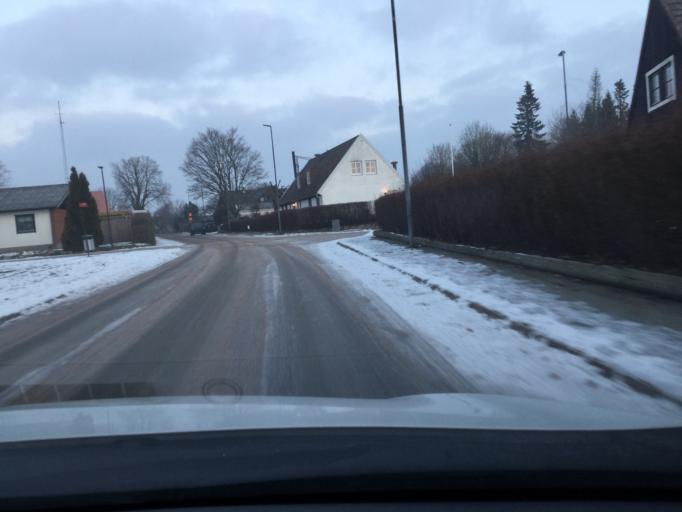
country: SE
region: Skane
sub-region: Hoors Kommun
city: Loberod
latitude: 55.7735
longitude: 13.5116
